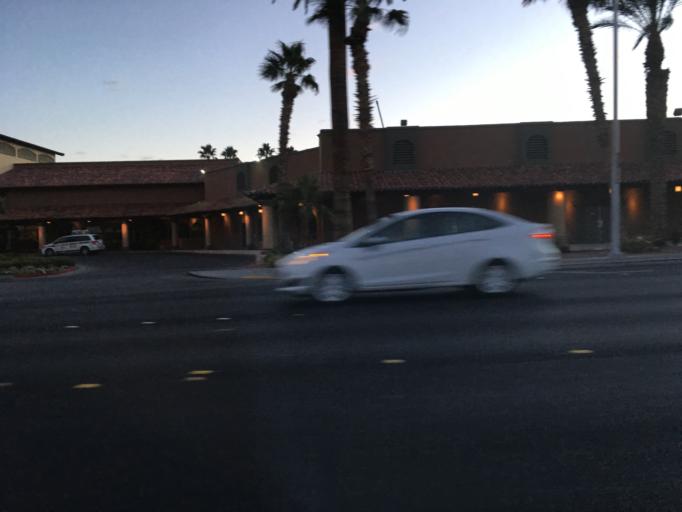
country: US
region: Nevada
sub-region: Clark County
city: Paradise
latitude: 36.1081
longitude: -115.1566
